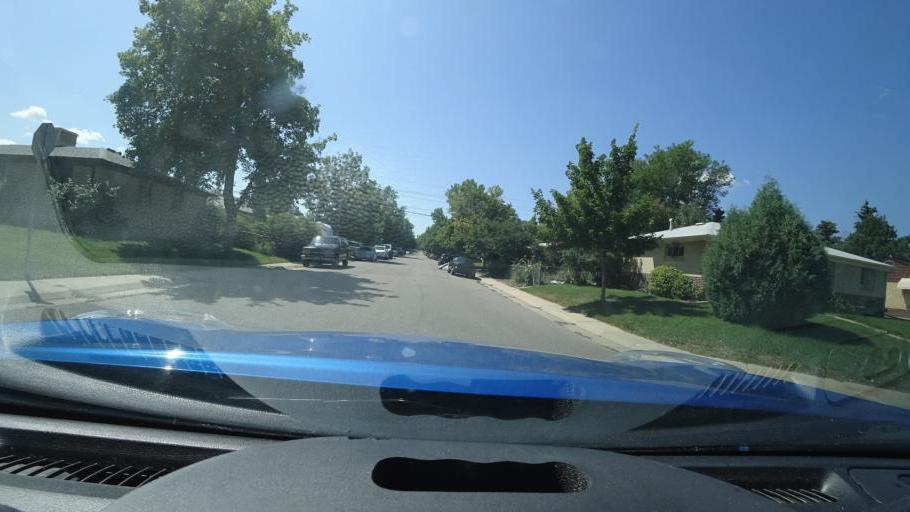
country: US
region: Colorado
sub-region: Adams County
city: Aurora
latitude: 39.7230
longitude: -104.8733
